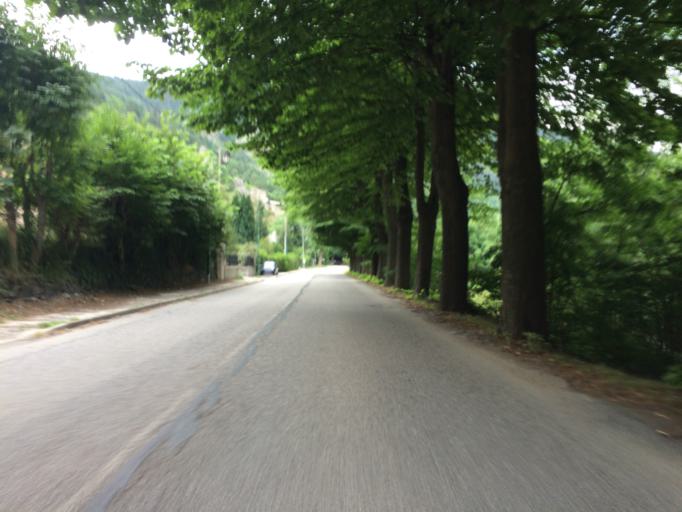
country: FR
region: Provence-Alpes-Cote d'Azur
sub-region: Departement des Alpes-Maritimes
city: Tende
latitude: 44.0802
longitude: 7.5979
